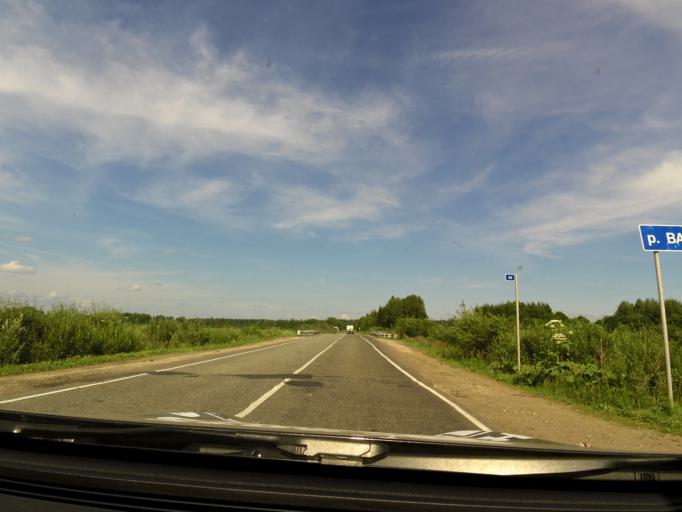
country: RU
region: Kirov
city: Slobodskoy
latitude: 58.7841
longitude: 50.4961
